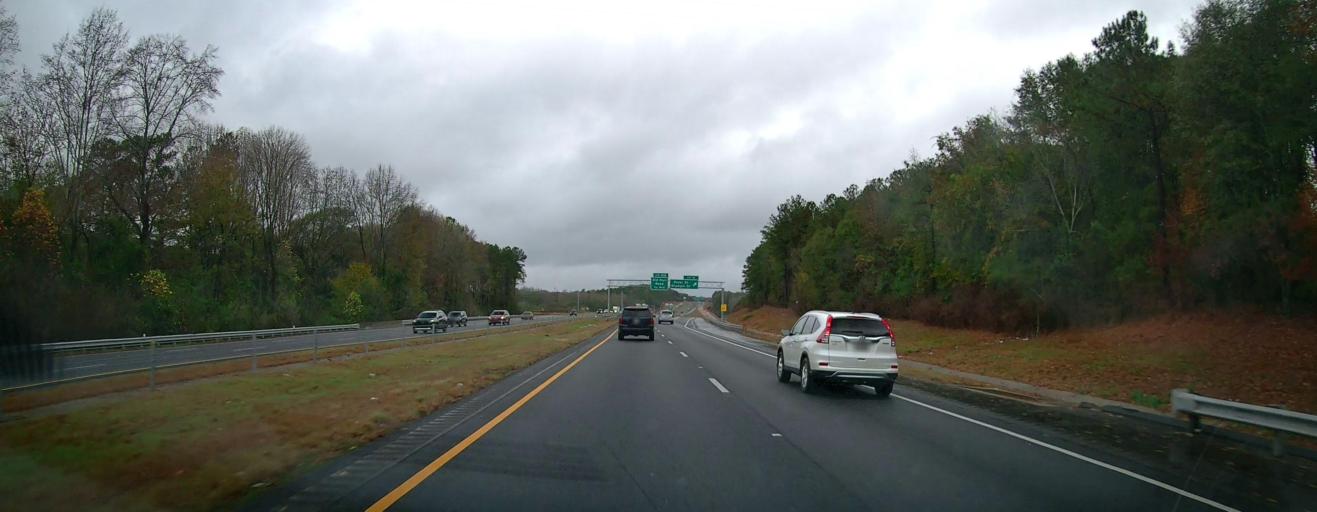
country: US
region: Georgia
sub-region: Clarke County
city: Athens
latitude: 33.9571
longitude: -83.3502
